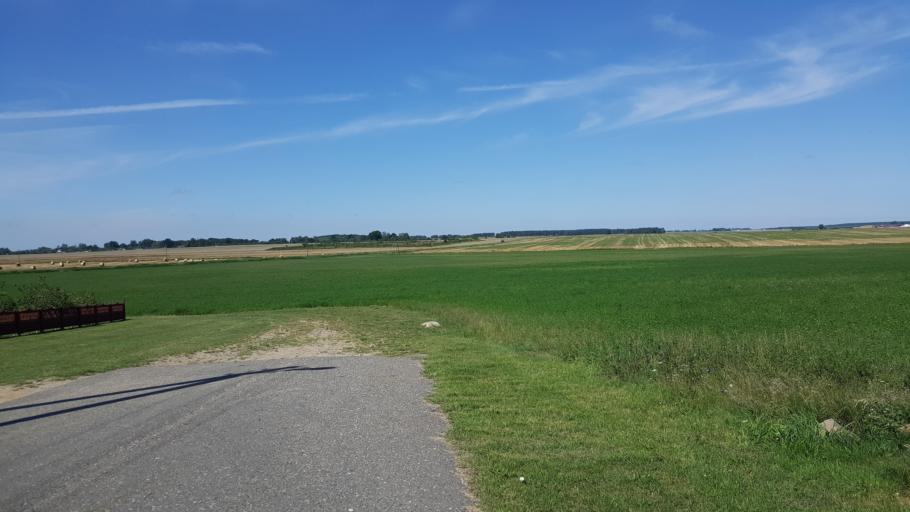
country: BY
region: Brest
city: Charnawchytsy
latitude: 52.2747
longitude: 23.7571
